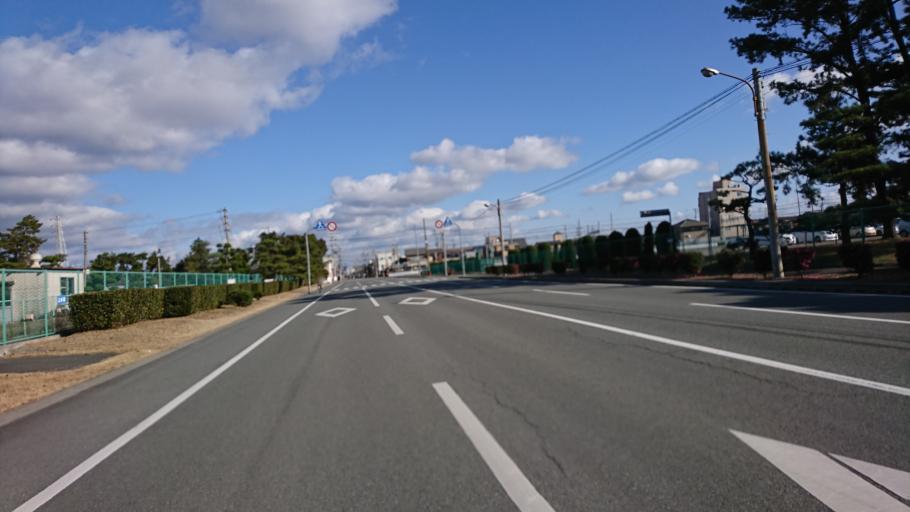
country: JP
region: Hyogo
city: Kakogawacho-honmachi
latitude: 34.7579
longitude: 134.7911
